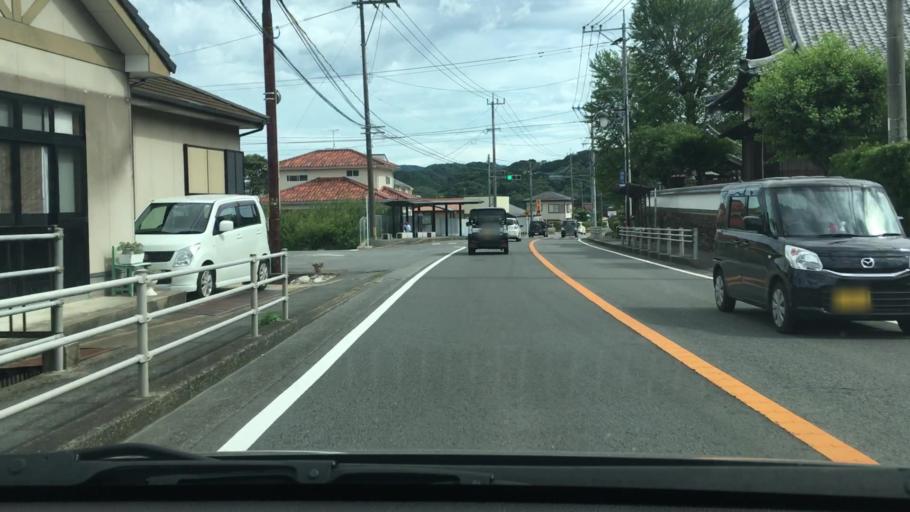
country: JP
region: Nagasaki
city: Togitsu
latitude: 32.9001
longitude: 129.7808
